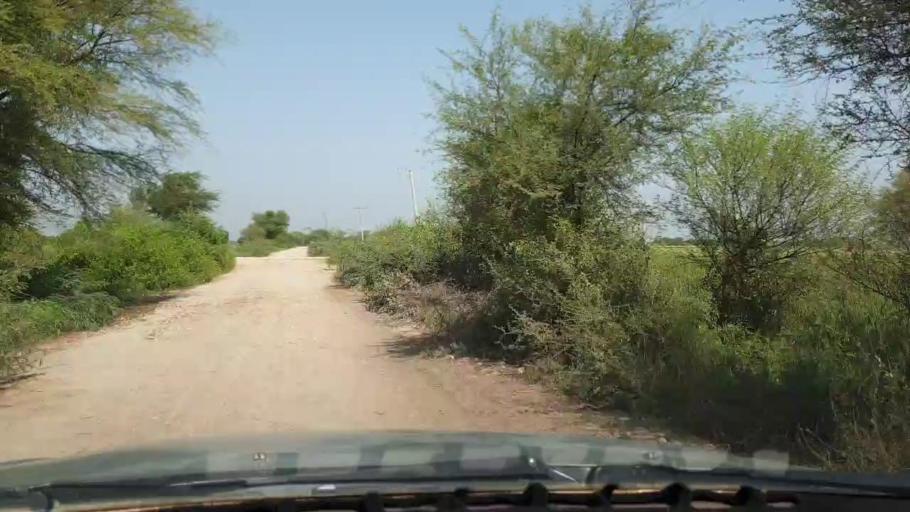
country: PK
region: Sindh
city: Tando Muhammad Khan
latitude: 25.1502
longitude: 68.6338
